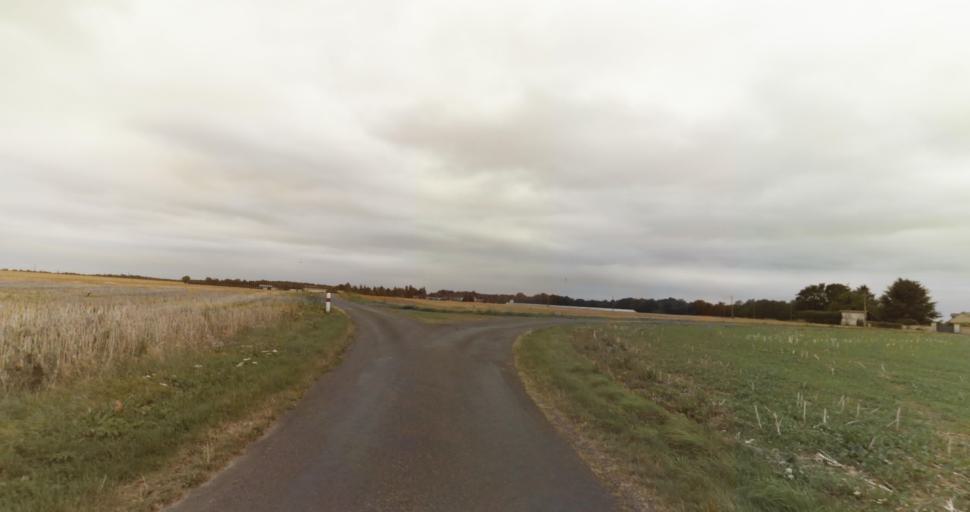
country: FR
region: Haute-Normandie
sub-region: Departement de l'Eure
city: La Couture-Boussey
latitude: 48.9207
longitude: 1.3596
